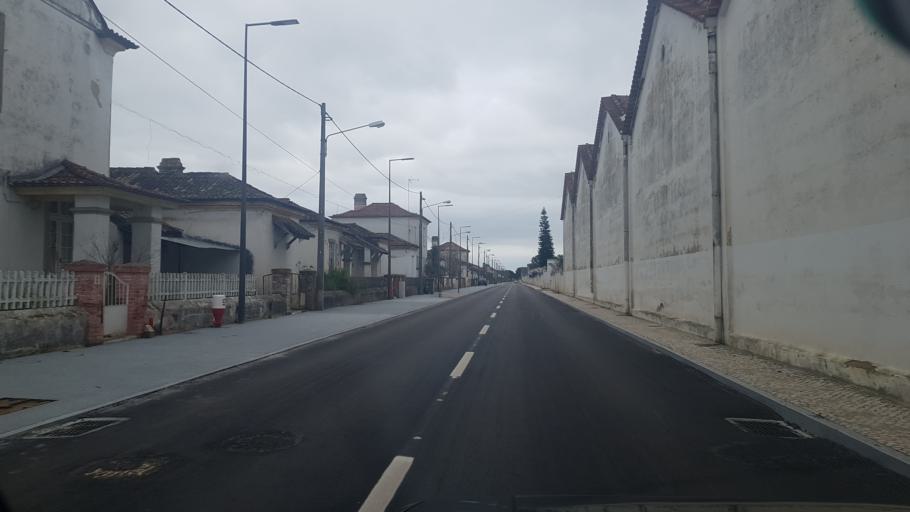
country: PT
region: Santarem
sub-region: Entroncamento
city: Entroncamento
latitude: 39.4635
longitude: -8.4760
